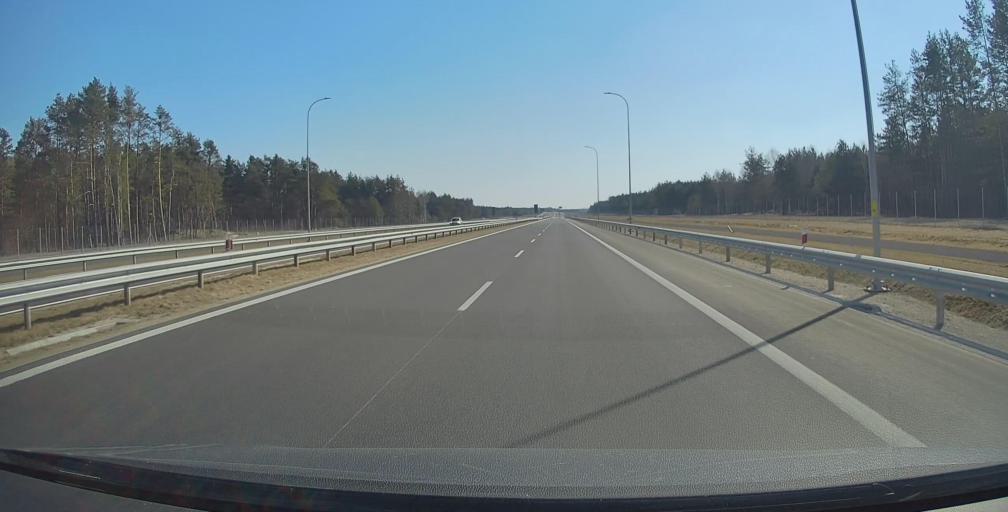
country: PL
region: Subcarpathian Voivodeship
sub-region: Powiat nizanski
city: Jezowe
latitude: 50.3832
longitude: 22.1652
